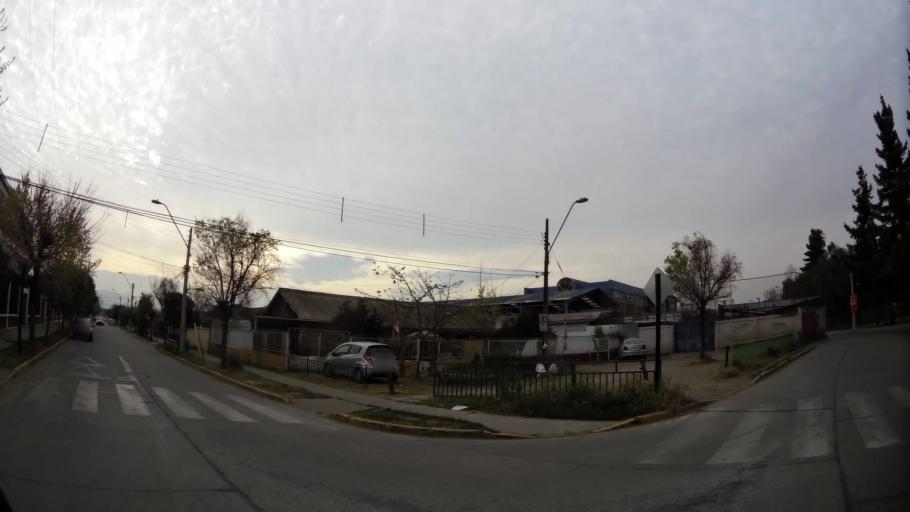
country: CL
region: Santiago Metropolitan
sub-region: Provincia de Santiago
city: Lo Prado
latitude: -33.5106
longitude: -70.7673
